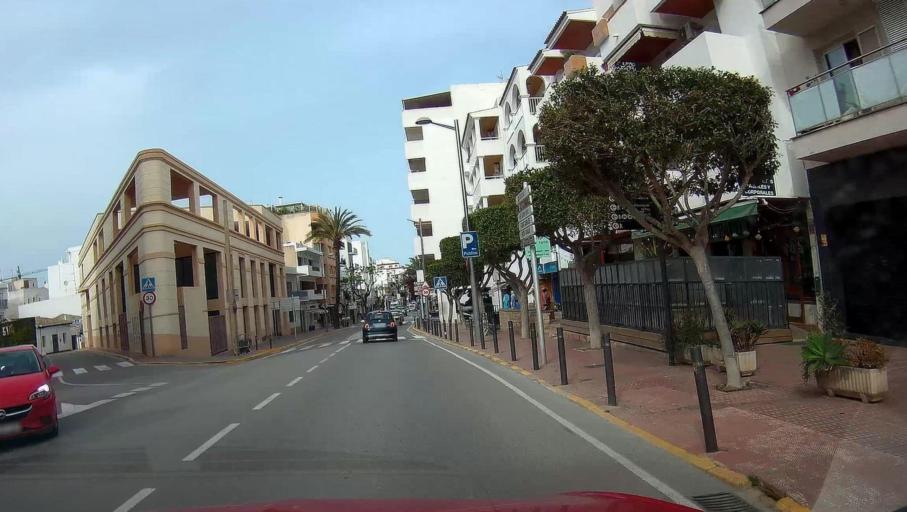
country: ES
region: Balearic Islands
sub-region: Illes Balears
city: Santa Eularia des Riu
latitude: 38.9839
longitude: 1.5322
